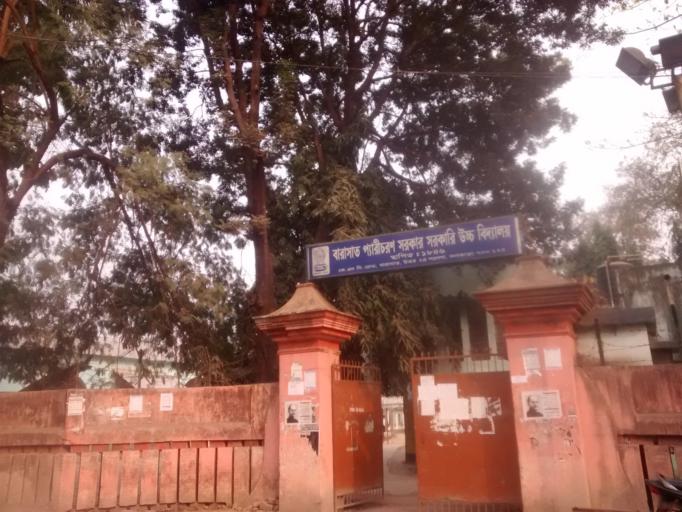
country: IN
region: West Bengal
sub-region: North 24 Parganas
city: Barasat
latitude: 22.7162
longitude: 88.4797
